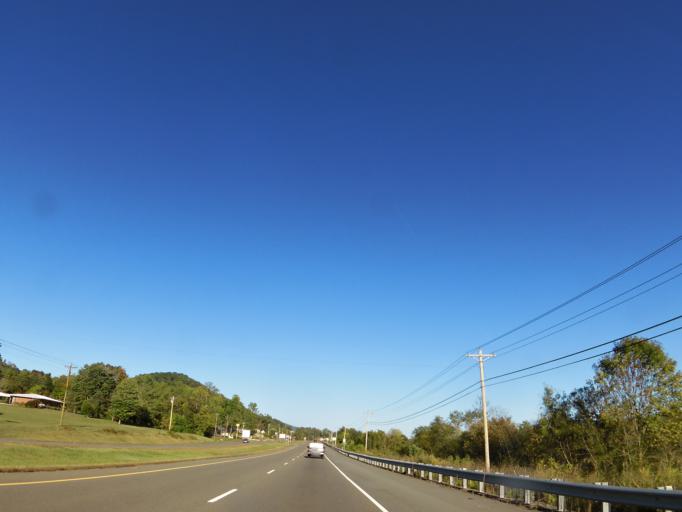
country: US
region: Tennessee
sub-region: Grainger County
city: Bean Station
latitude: 36.3454
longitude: -83.3204
